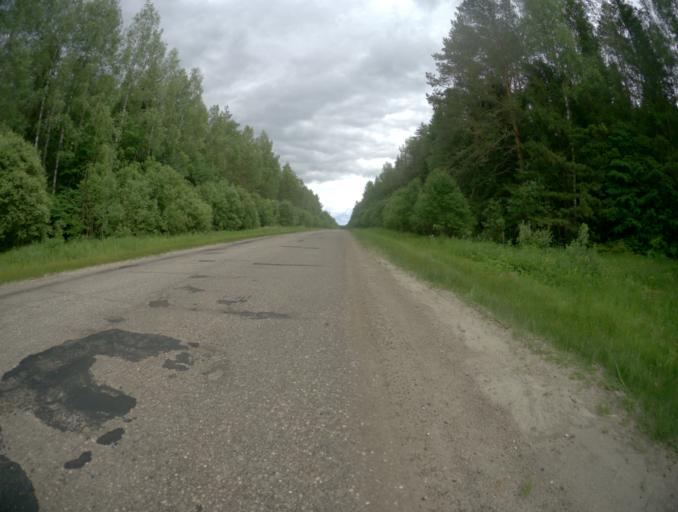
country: RU
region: Ivanovo
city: Arkhipovka
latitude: 56.6234
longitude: 41.3053
